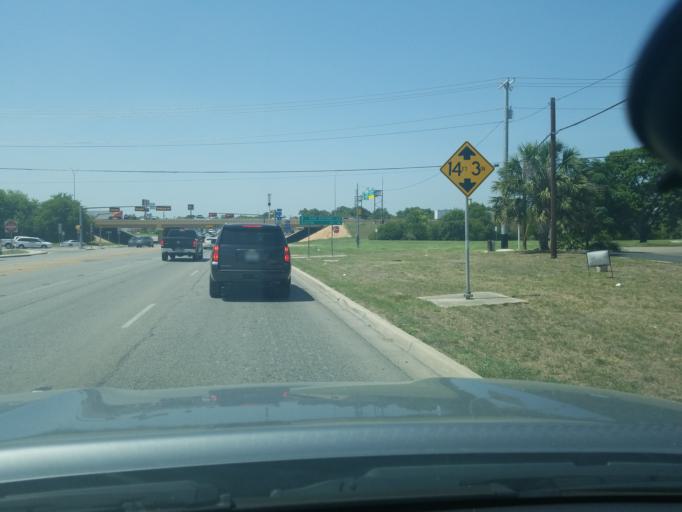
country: US
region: Texas
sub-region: Comal County
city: New Braunfels
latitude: 29.6904
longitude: -98.1092
